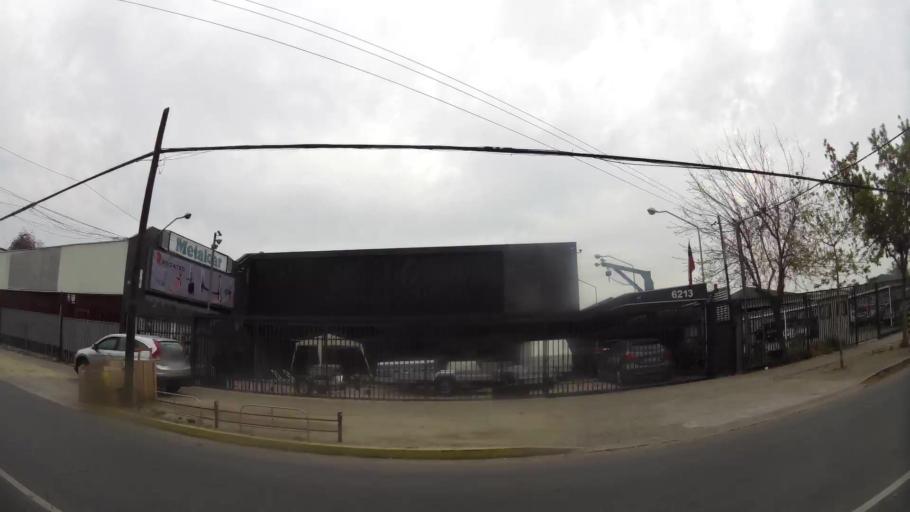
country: CL
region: Santiago Metropolitan
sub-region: Provincia de Santiago
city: Villa Presidente Frei, Nunoa, Santiago, Chile
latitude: -33.4810
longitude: -70.6061
